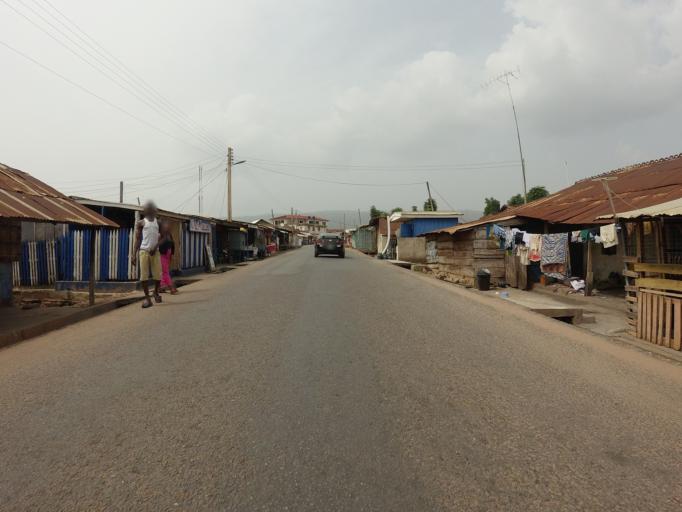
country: GH
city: Akropong
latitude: 6.1043
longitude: -0.0124
